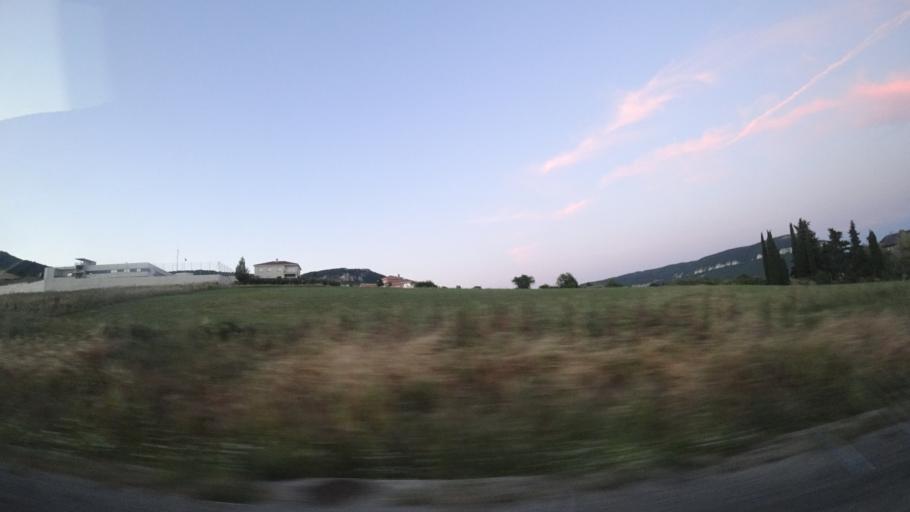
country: FR
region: Midi-Pyrenees
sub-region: Departement de l'Aveyron
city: Millau
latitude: 44.1179
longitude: 3.0638
